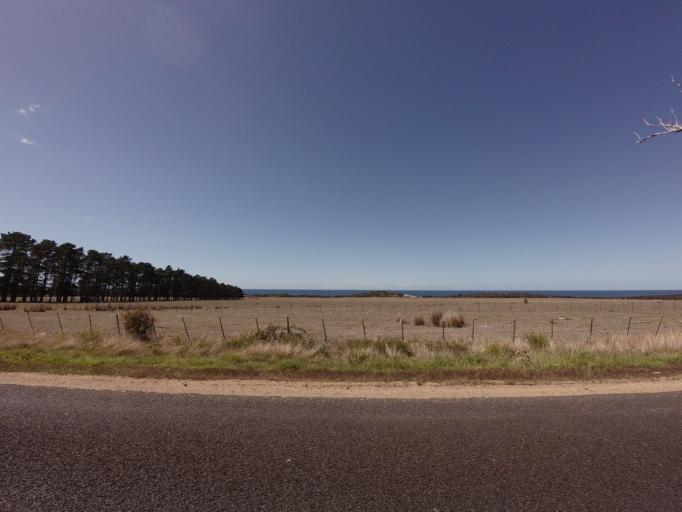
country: AU
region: Tasmania
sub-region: Break O'Day
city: St Helens
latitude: -41.7107
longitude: 148.2746
